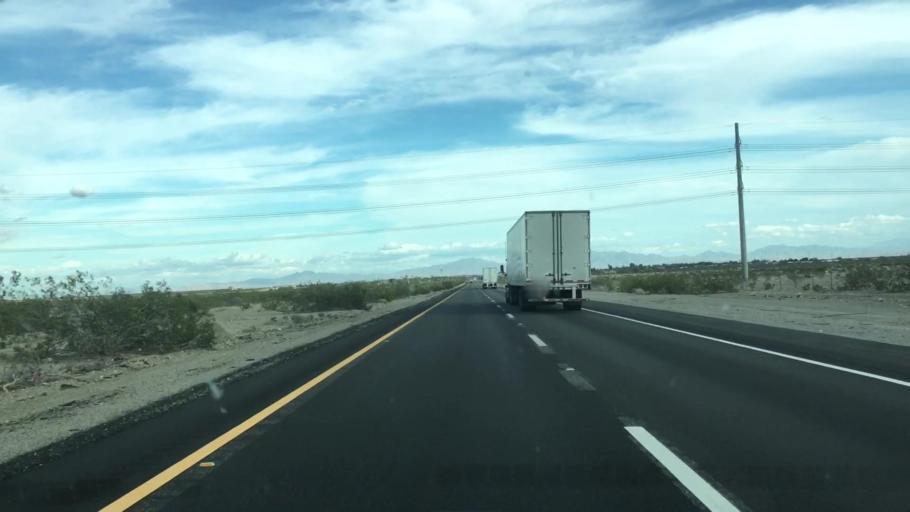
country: US
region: California
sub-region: Riverside County
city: Mesa Verde
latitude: 33.6088
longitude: -114.7549
